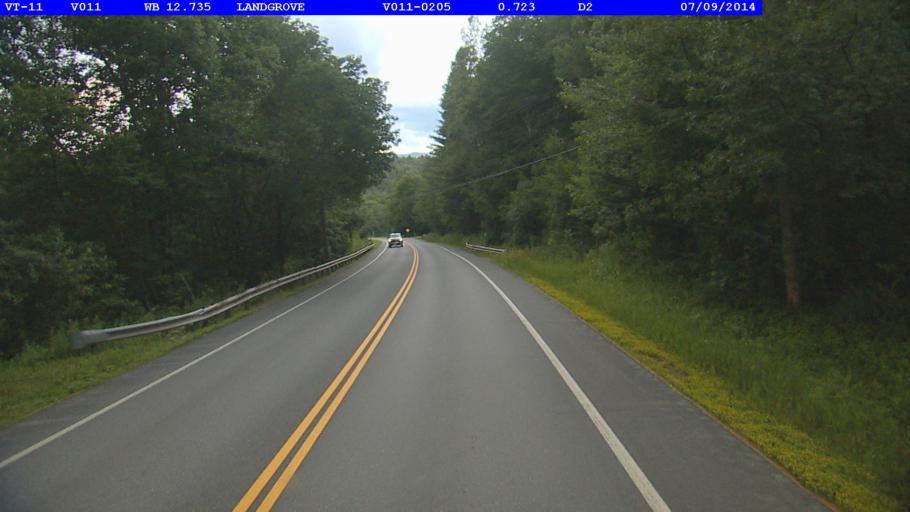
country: US
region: Vermont
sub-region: Bennington County
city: Manchester Center
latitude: 43.2370
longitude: -72.8517
